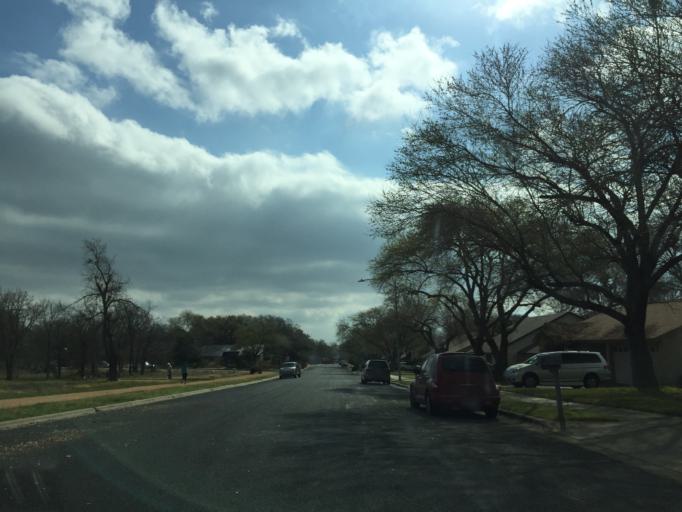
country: US
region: Texas
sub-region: Williamson County
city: Jollyville
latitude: 30.4125
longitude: -97.7388
